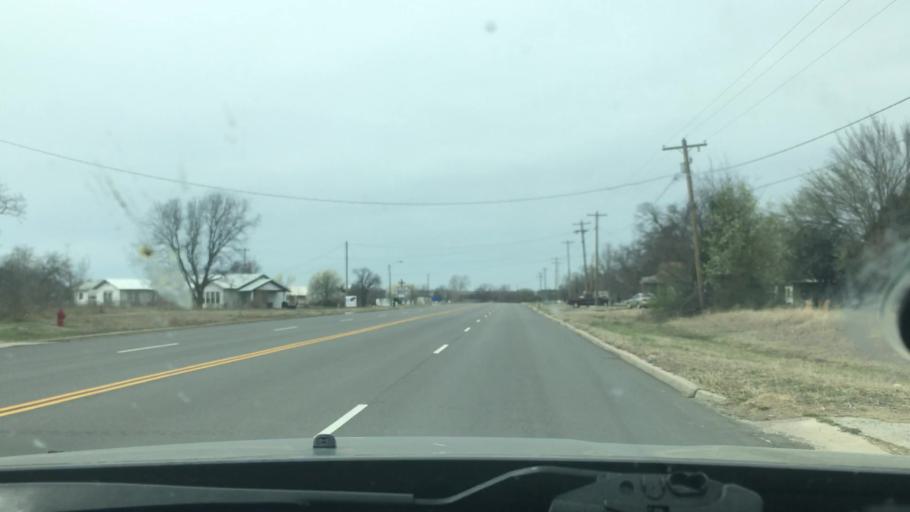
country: US
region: Oklahoma
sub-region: Seminole County
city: Seminole
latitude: 35.2592
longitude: -96.7112
